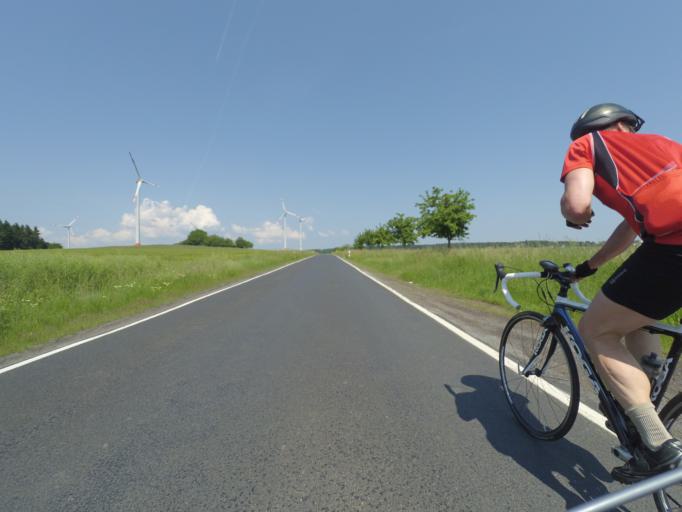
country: DE
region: Rheinland-Pfalz
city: Reudelsterz
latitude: 50.3230
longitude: 7.1500
